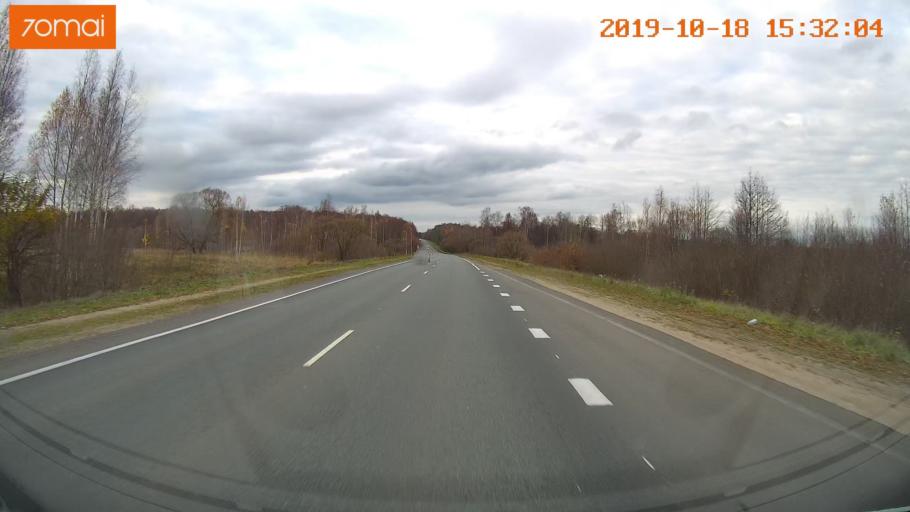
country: RU
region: Vladimir
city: Anopino
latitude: 55.8213
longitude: 40.6597
